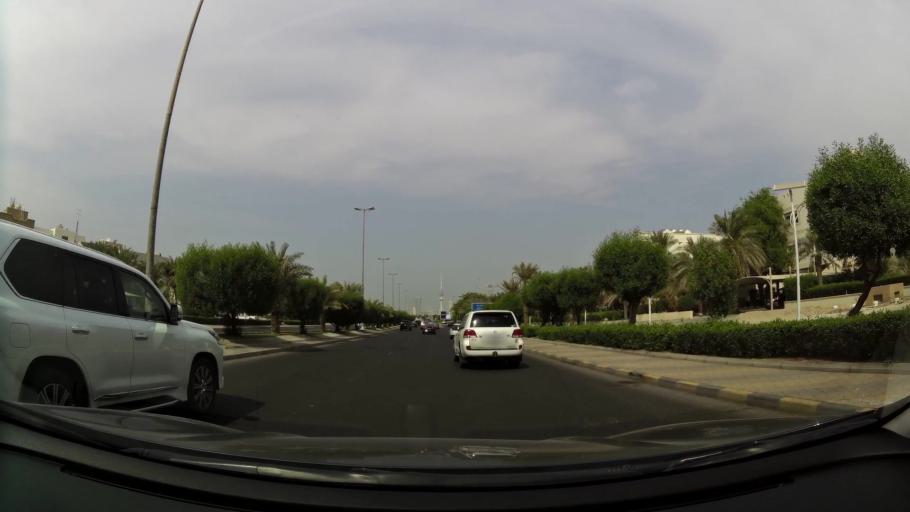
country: KW
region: Al Asimah
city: Ash Shamiyah
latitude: 29.3373
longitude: 47.9866
